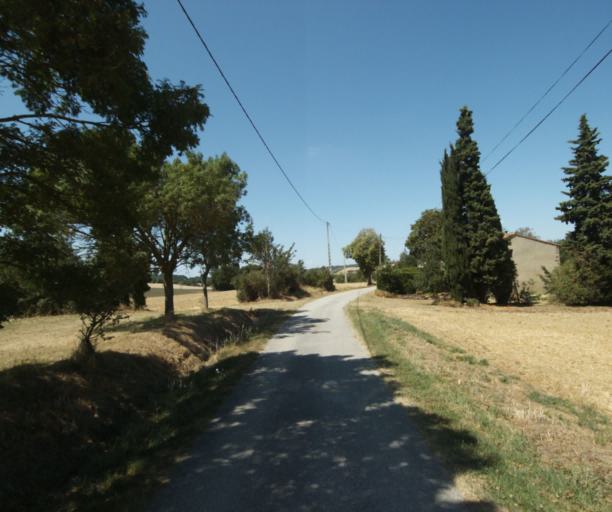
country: FR
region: Midi-Pyrenees
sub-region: Departement de la Haute-Garonne
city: Saint-Felix-Lauragais
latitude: 43.4755
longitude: 1.8797
